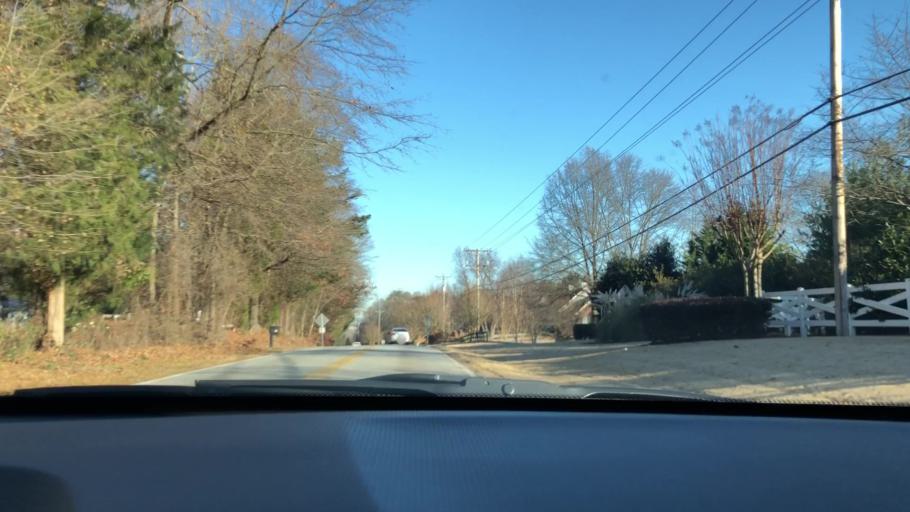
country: US
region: South Carolina
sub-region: Greenville County
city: Five Forks
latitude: 34.8343
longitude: -82.2275
